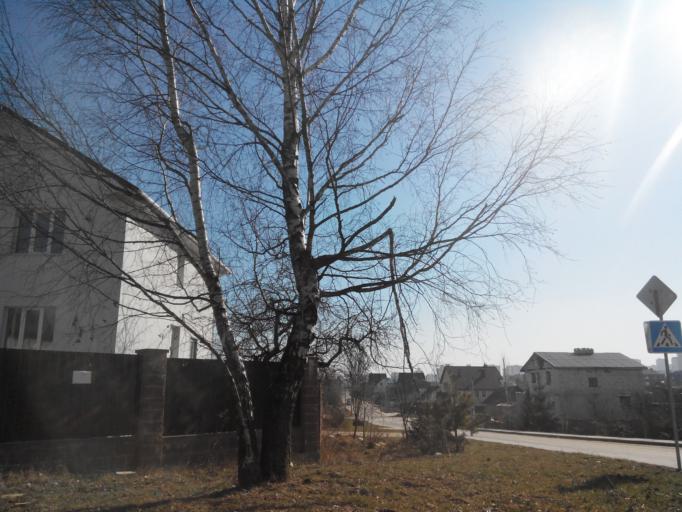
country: BY
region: Minsk
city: Zhdanovichy
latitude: 53.9238
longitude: 27.4074
